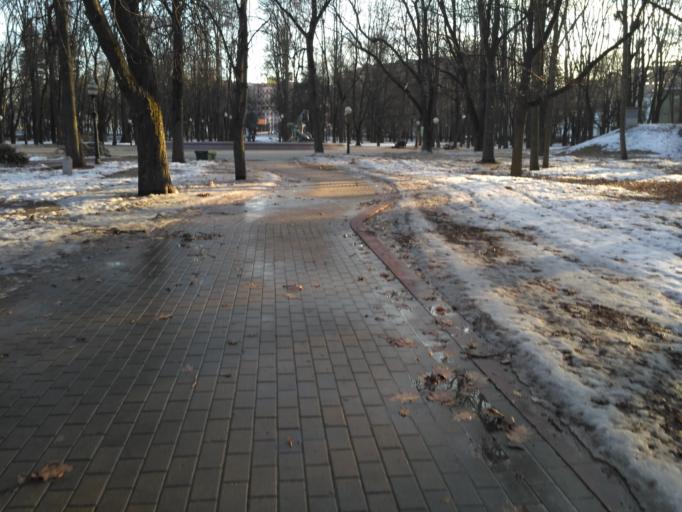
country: BY
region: Minsk
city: Minsk
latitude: 53.9072
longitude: 27.5668
